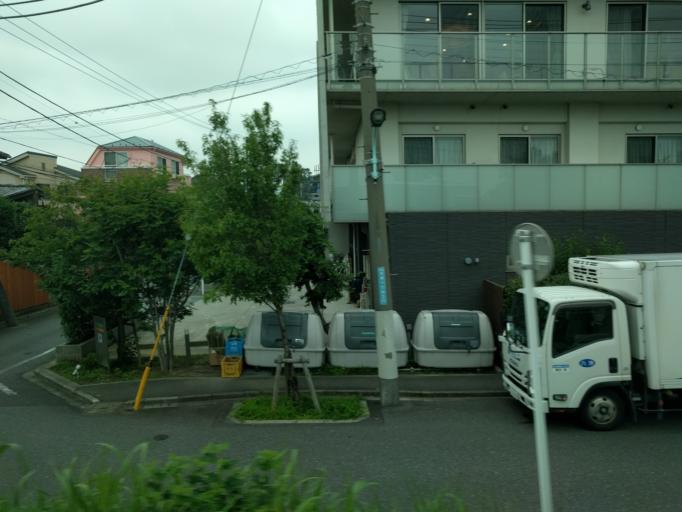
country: JP
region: Kanagawa
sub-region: Kawasaki-shi
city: Kawasaki
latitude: 35.5929
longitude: 139.6560
